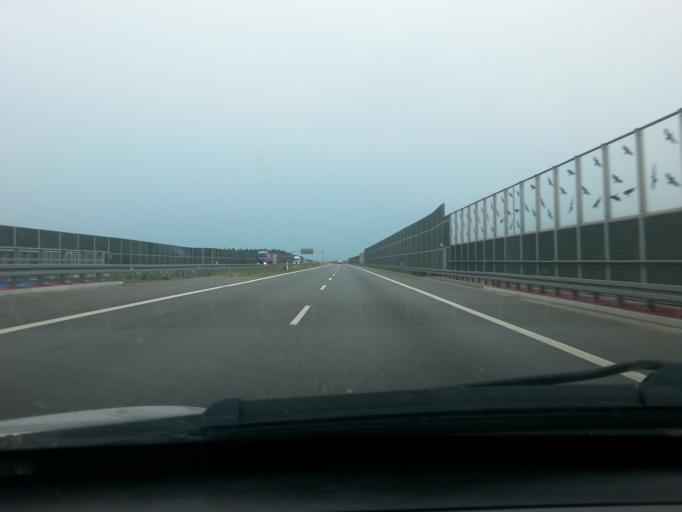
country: PL
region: Lodz Voivodeship
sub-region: powiat Lowicki
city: Bobrowniki
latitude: 52.0394
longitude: 20.0318
